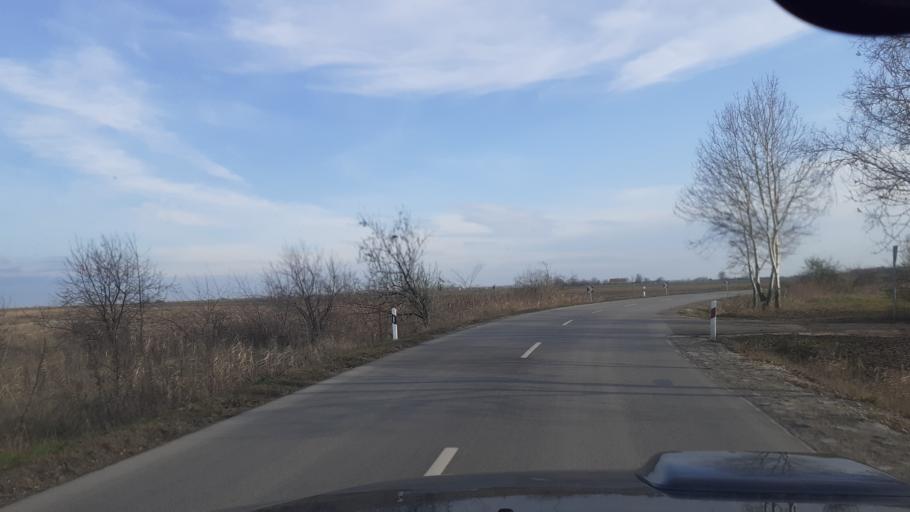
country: HU
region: Bacs-Kiskun
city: Kunszentmiklos
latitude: 47.0487
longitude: 19.1165
